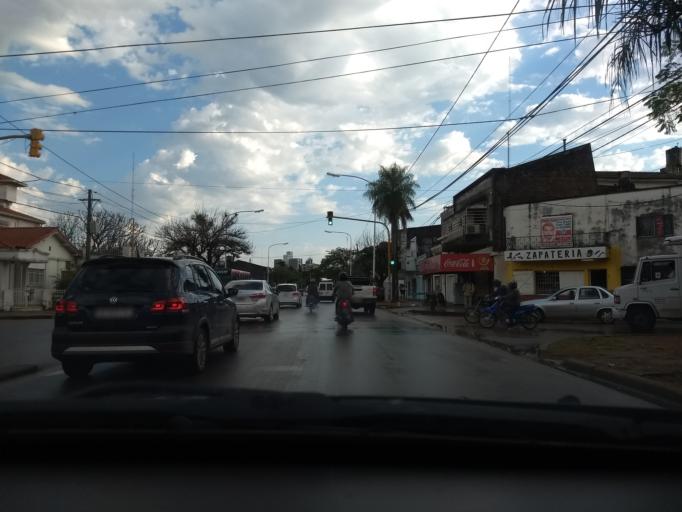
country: AR
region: Corrientes
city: Corrientes
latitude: -27.4794
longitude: -58.8286
